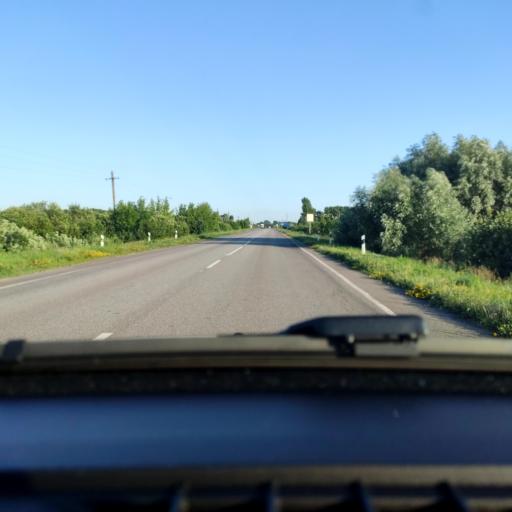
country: RU
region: Voronezj
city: Kashirskoye
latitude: 51.4725
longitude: 39.8614
